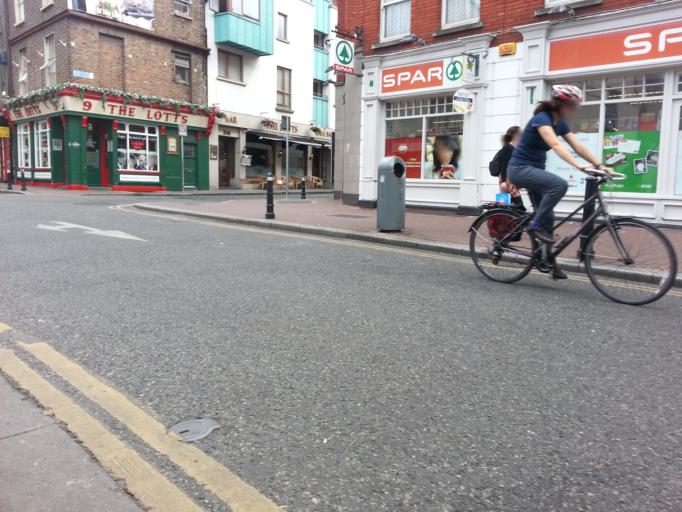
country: IE
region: Leinster
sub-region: Dublin City
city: Dublin
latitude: 53.3471
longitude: -6.2634
